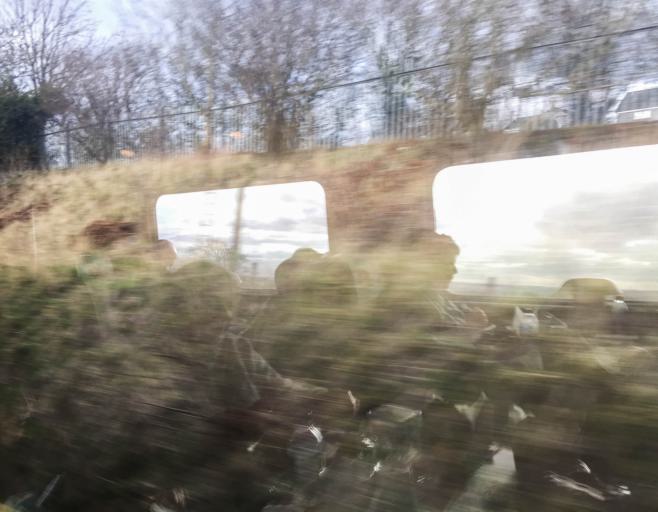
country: GB
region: Scotland
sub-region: South Lanarkshire
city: Carluke
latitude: 55.7343
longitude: -3.8547
